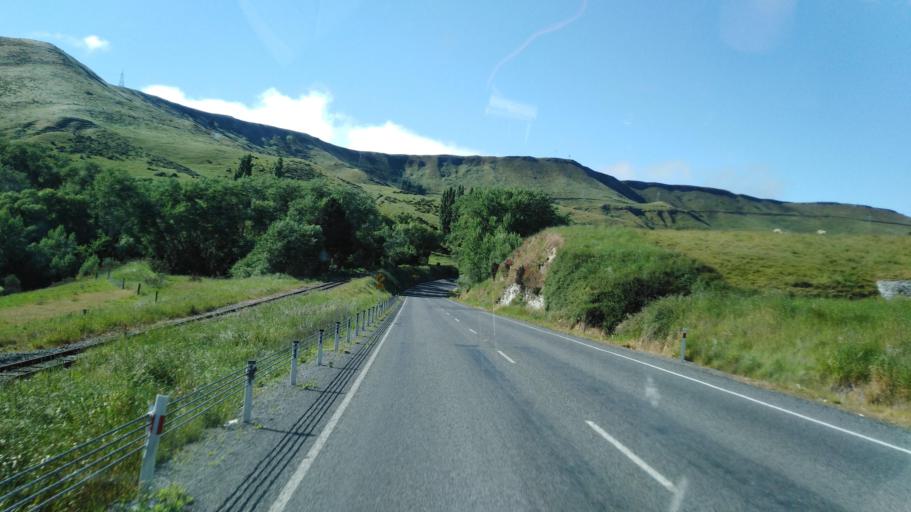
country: NZ
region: Canterbury
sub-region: Hurunui District
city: Amberley
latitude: -42.9853
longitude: 172.7193
